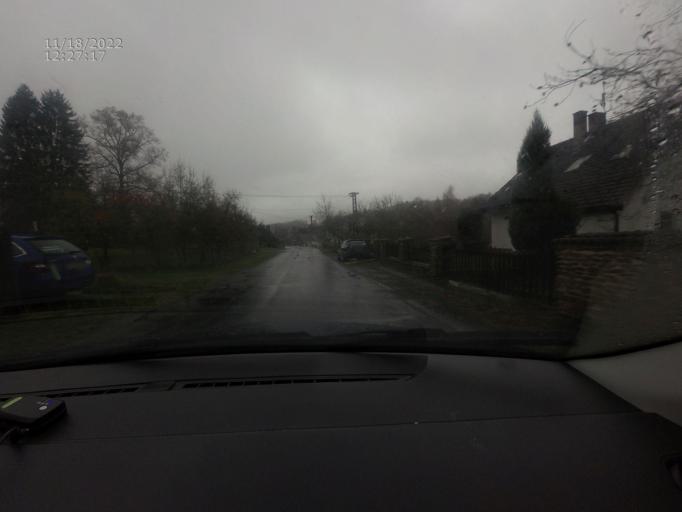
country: CZ
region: Plzensky
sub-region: Okres Klatovy
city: Planice
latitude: 49.4278
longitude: 13.5046
